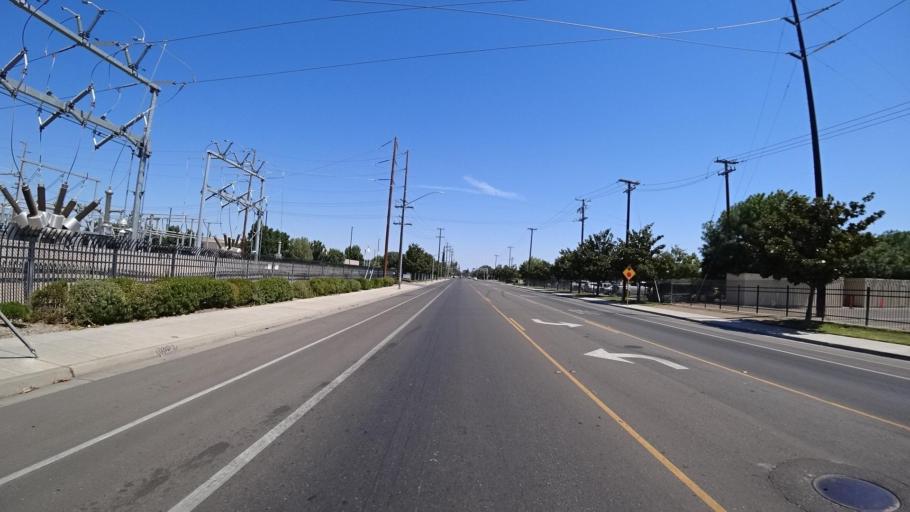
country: US
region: California
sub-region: Fresno County
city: Fresno
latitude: 36.7195
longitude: -119.7637
